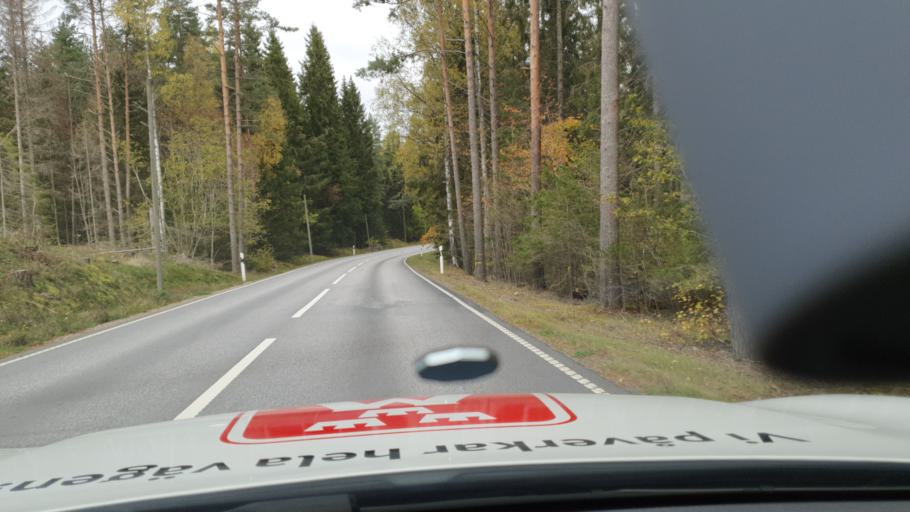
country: SE
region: OErebro
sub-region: Hallsbergs Kommun
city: Palsboda
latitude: 58.8177
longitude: 15.4133
